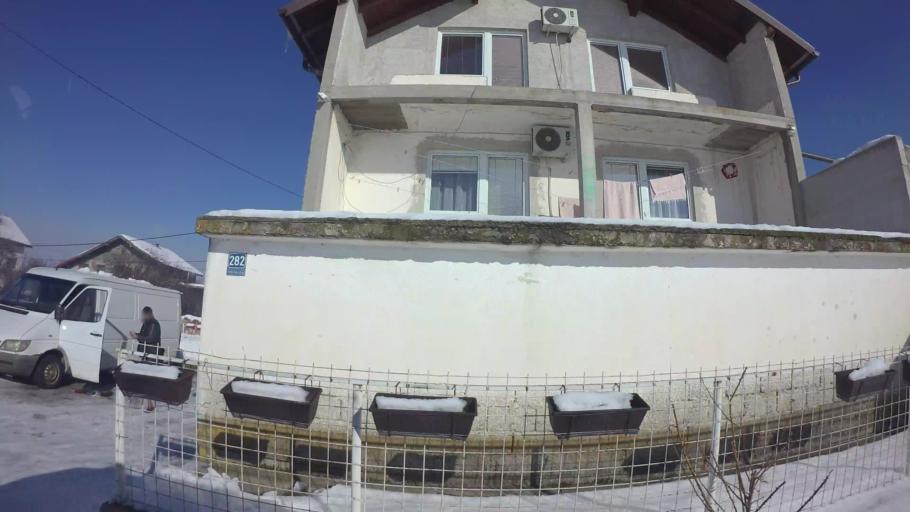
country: BA
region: Federation of Bosnia and Herzegovina
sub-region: Kanton Sarajevo
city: Sarajevo
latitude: 43.7997
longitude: 18.3348
